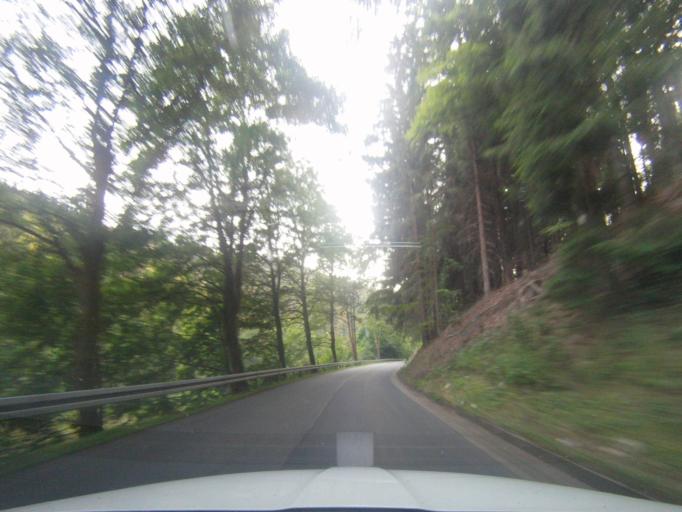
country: DE
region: Thuringia
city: Eisfeld
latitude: 50.4848
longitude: 10.8992
